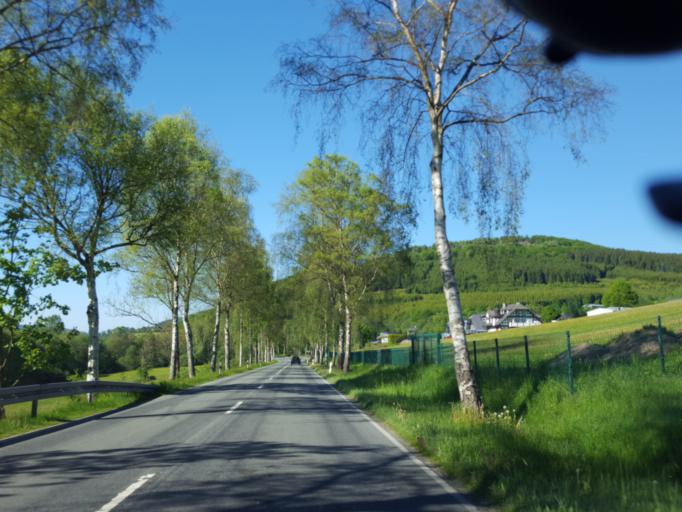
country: DE
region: North Rhine-Westphalia
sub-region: Regierungsbezirk Arnsberg
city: Winterberg
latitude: 51.2358
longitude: 8.4835
